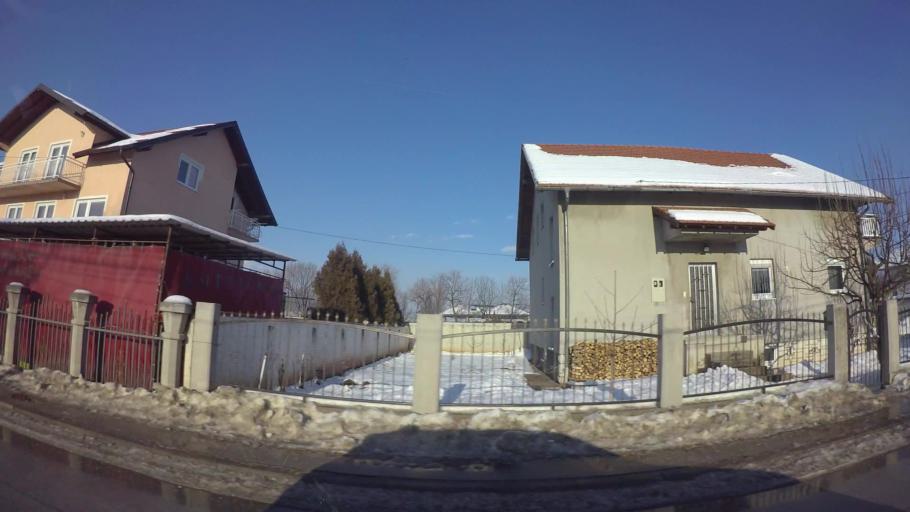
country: BA
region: Federation of Bosnia and Herzegovina
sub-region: Kanton Sarajevo
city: Sarajevo
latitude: 43.8168
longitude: 18.3354
